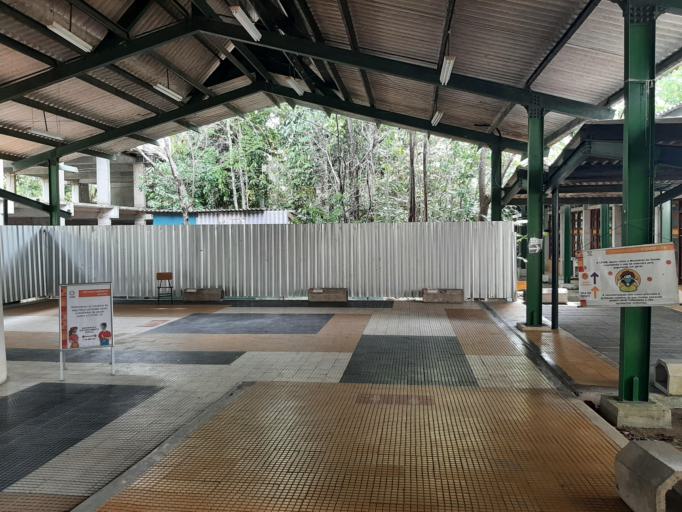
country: BR
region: Amazonas
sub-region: Manaus
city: Manaus
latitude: -3.0912
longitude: -59.9625
